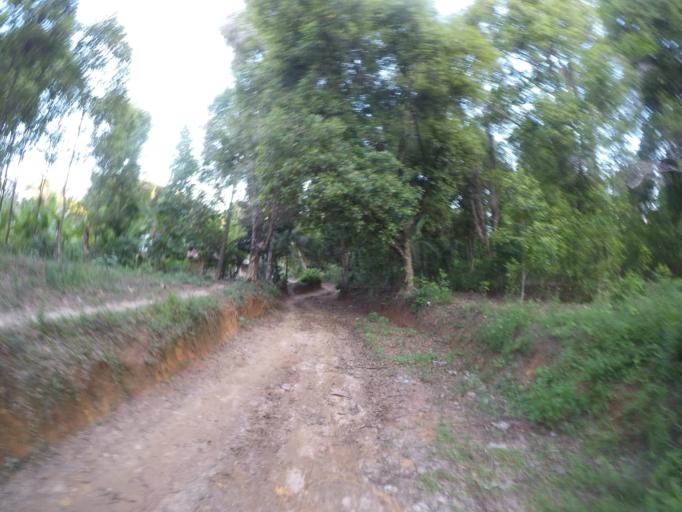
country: TZ
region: Pemba South
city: Mtambile
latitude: -5.3802
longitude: 39.7120
